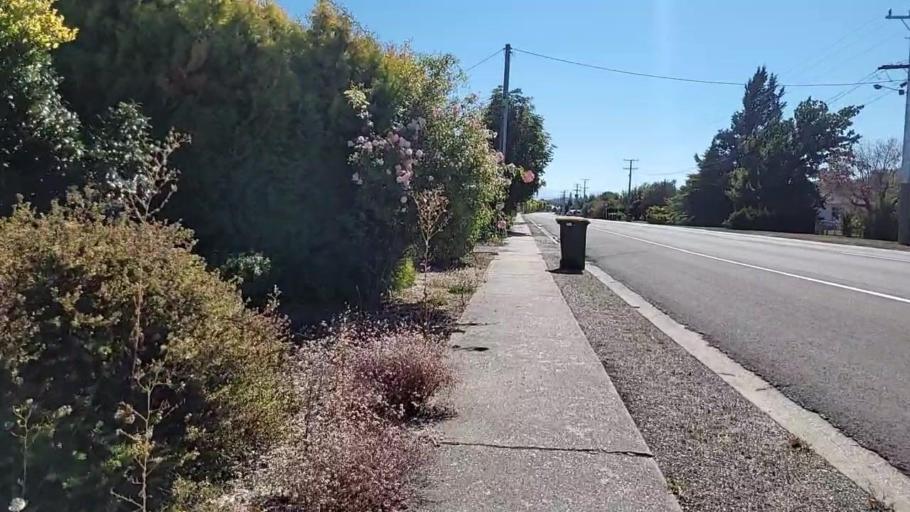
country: NZ
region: Otago
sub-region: Queenstown-Lakes District
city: Wanaka
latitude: -45.1017
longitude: 169.5961
